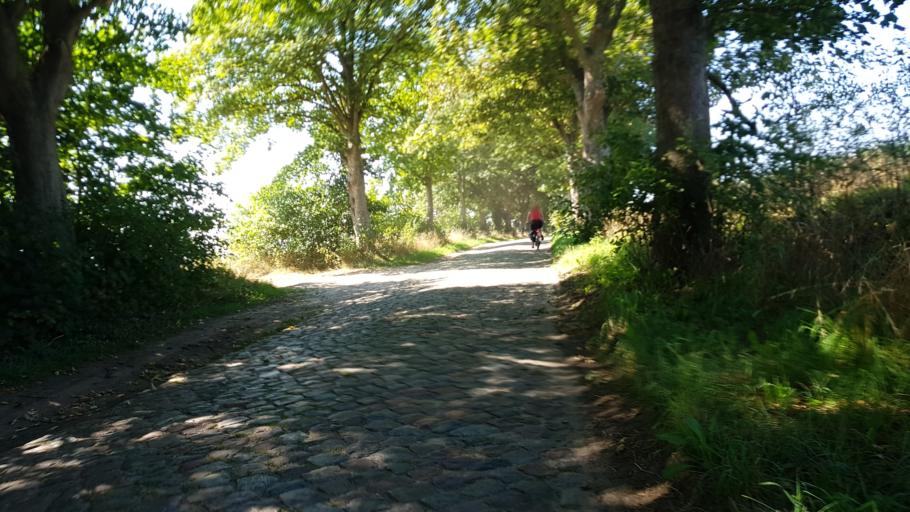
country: PL
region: West Pomeranian Voivodeship
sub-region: Powiat gryfinski
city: Gryfino
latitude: 53.1523
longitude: 14.5024
